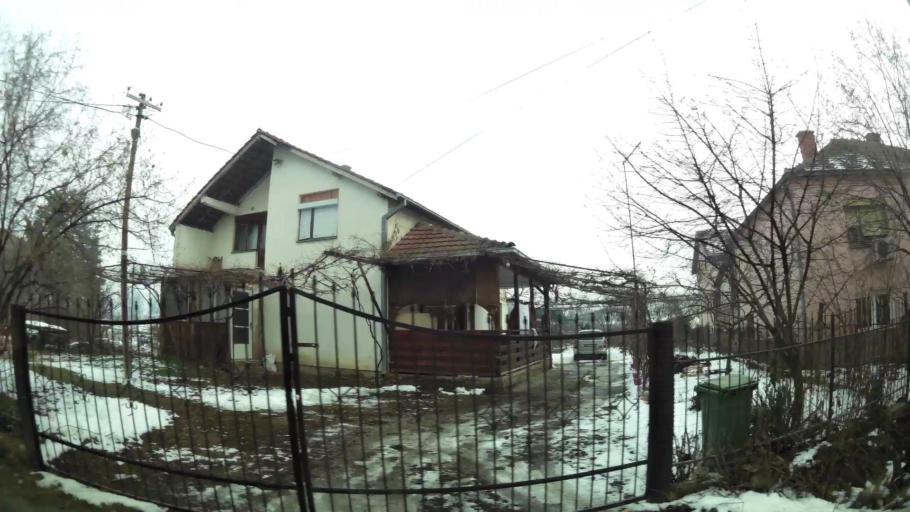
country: MK
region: Ilinden
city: Jurumleri
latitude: 41.9709
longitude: 21.5564
